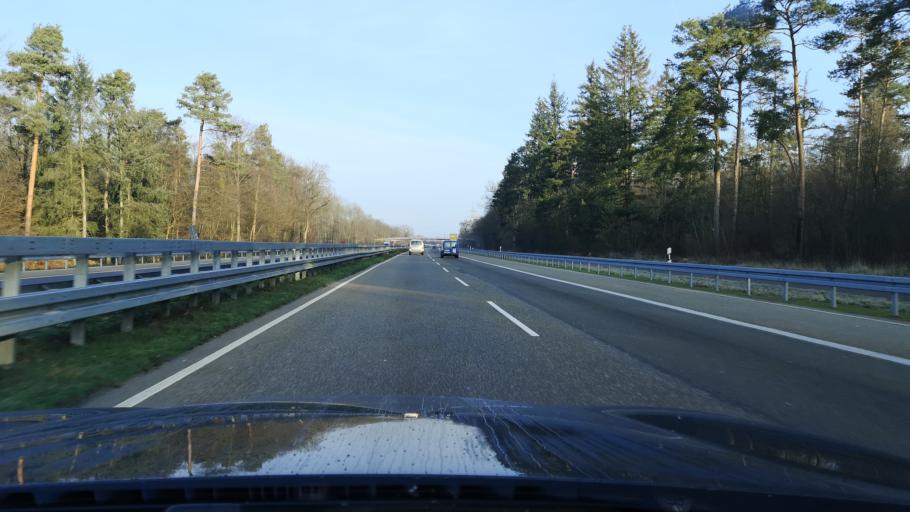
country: DE
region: Baden-Wuerttemberg
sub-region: Karlsruhe Region
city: Ettlingen
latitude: 48.9678
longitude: 8.3768
